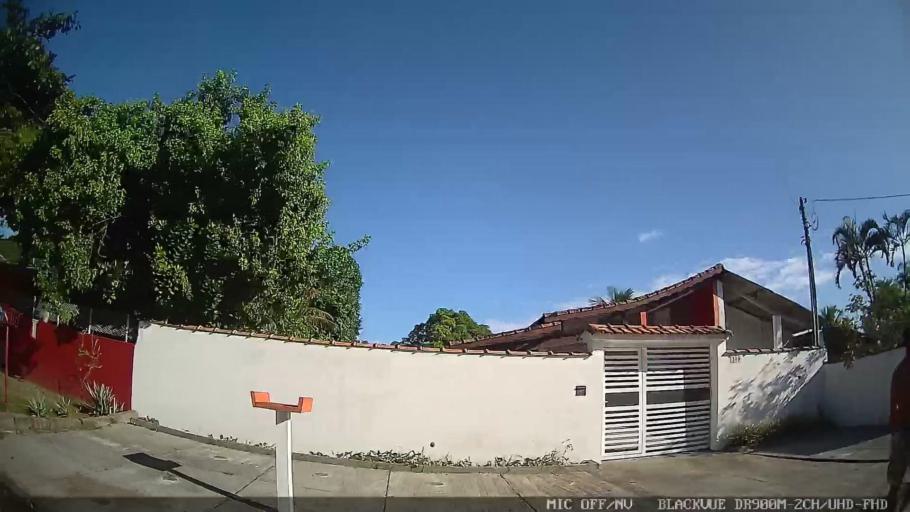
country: BR
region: Sao Paulo
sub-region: Peruibe
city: Peruibe
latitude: -24.2716
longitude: -46.9478
